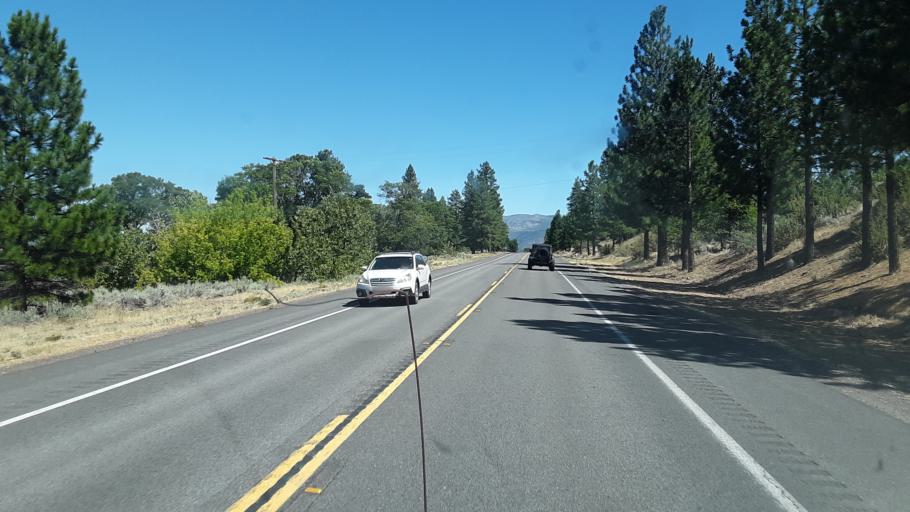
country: US
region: California
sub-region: Lassen County
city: Janesville
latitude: 40.2227
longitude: -120.4343
